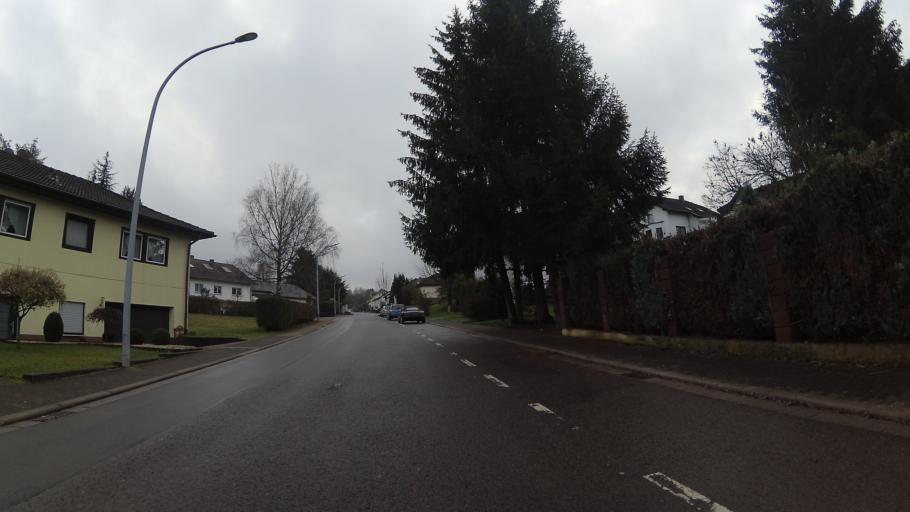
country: DE
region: Saarland
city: Spiesen-Elversberg
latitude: 49.3193
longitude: 7.1634
